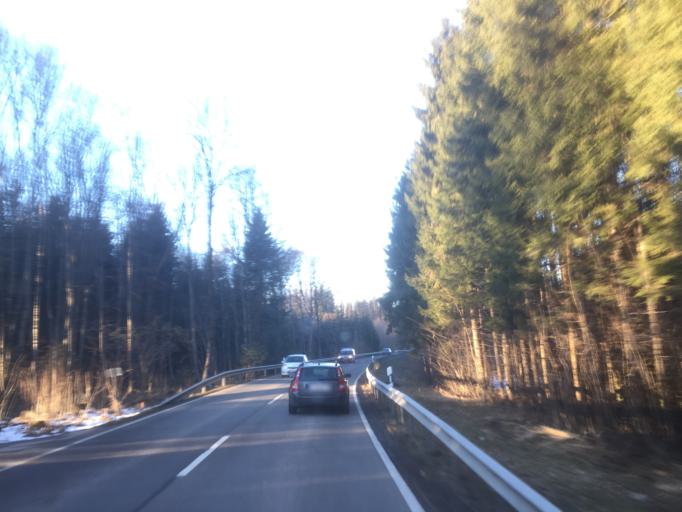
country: DE
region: Bavaria
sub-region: Upper Bavaria
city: Vachendorf
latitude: 47.8434
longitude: 12.6316
